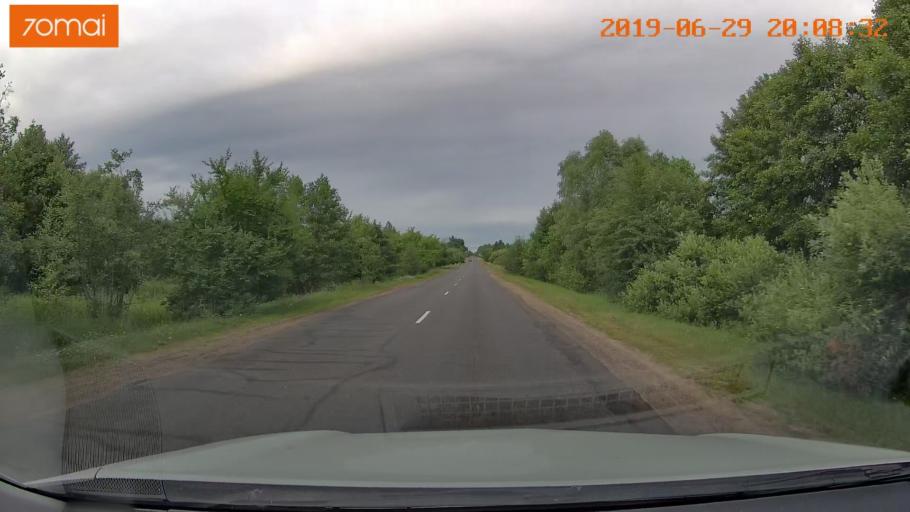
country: BY
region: Brest
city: Lahishyn
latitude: 52.3451
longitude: 26.0587
